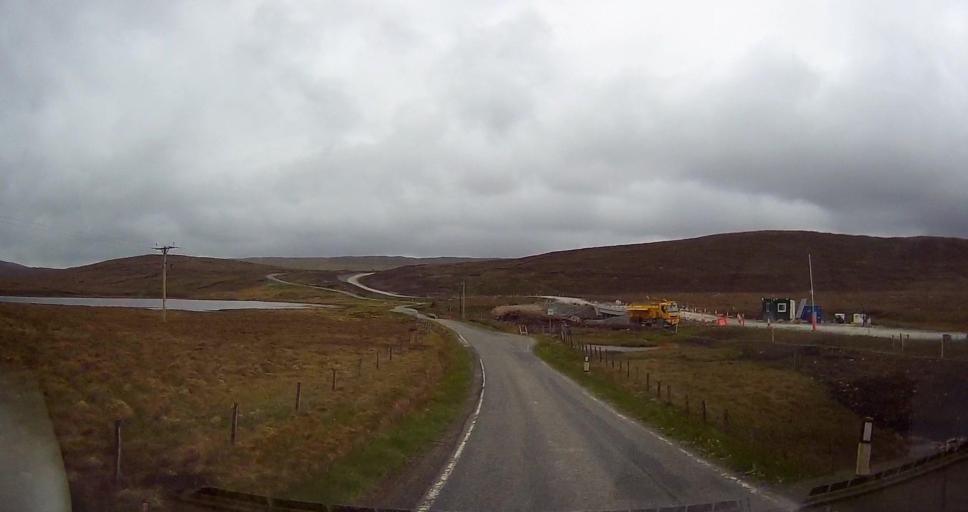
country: GB
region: Scotland
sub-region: Shetland Islands
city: Lerwick
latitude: 60.2794
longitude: -1.2484
